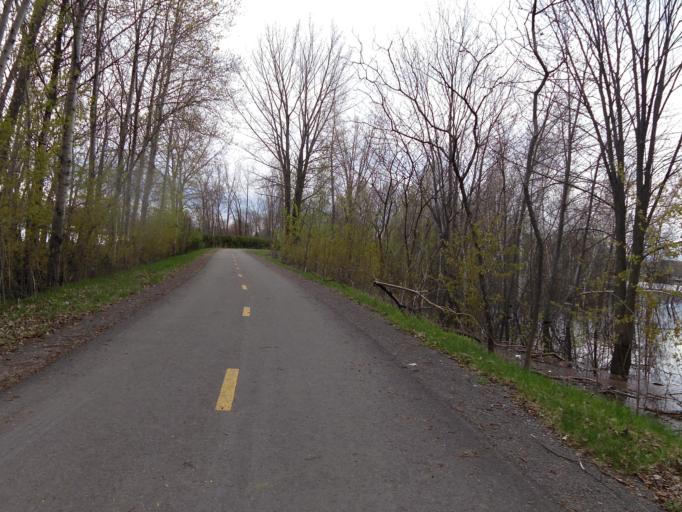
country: CA
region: Quebec
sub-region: Laurentides
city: Sainte-Marthe-sur-le-Lac
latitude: 45.5035
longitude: -73.9800
